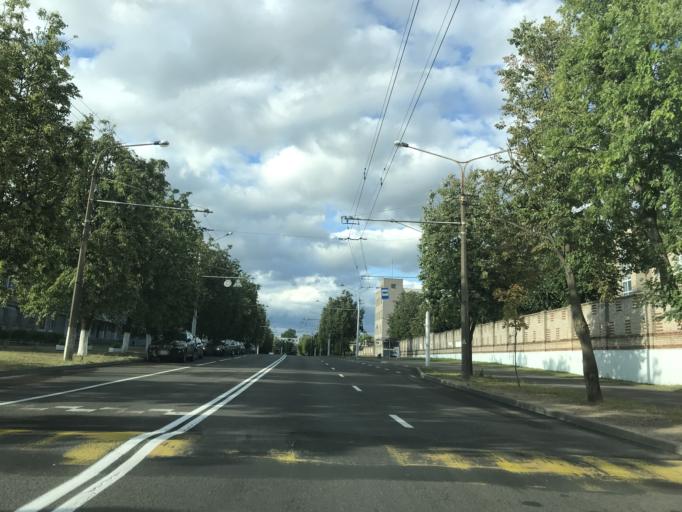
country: BY
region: Minsk
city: Minsk
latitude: 53.9445
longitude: 27.6216
